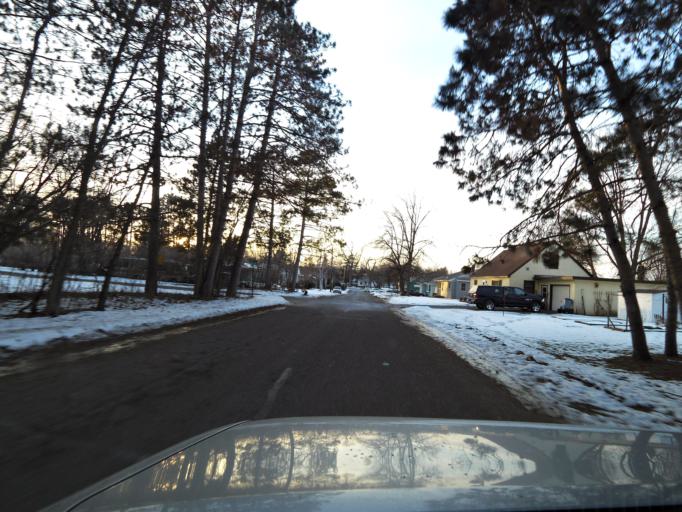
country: US
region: Wisconsin
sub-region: Saint Croix County
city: North Hudson
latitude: 44.9923
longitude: -92.7540
